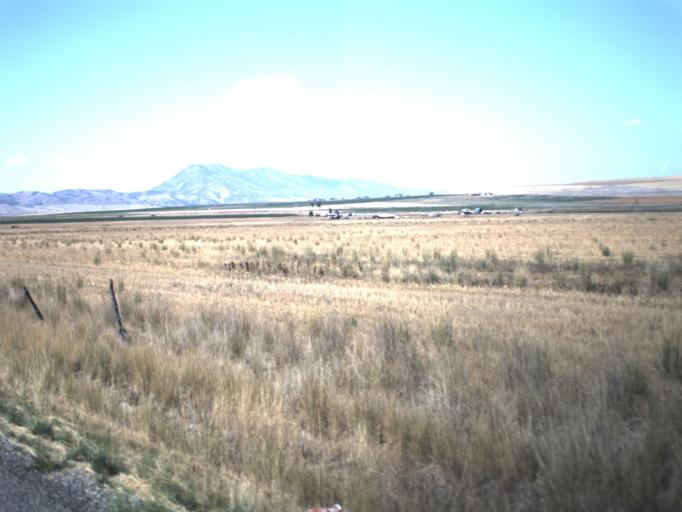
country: US
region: Utah
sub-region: Cache County
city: Benson
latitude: 41.8449
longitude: -111.9402
